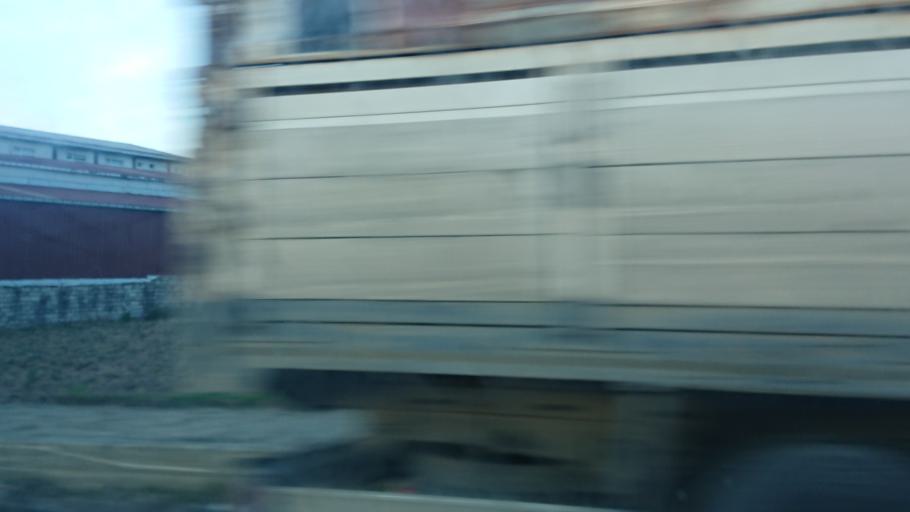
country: TR
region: Rize
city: Gundogdu
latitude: 41.0390
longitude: 40.5797
